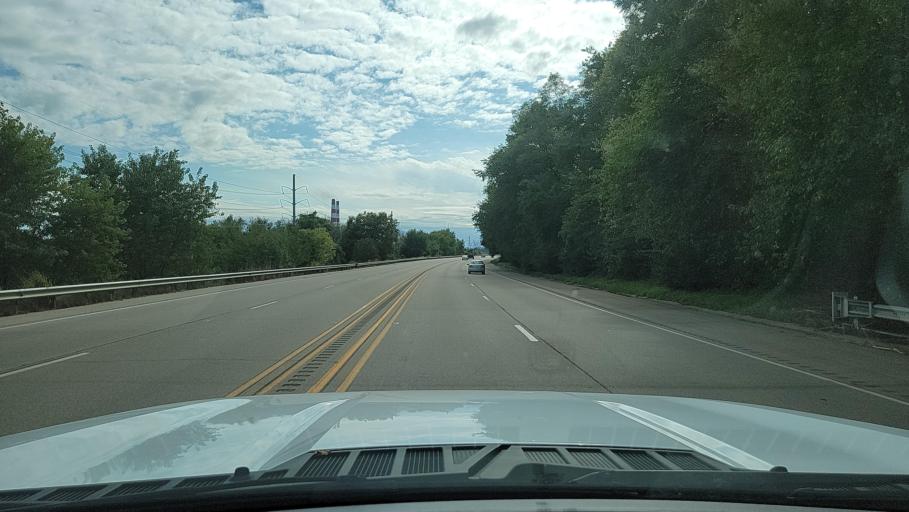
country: US
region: Illinois
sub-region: Tazewell County
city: North Pekin
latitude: 40.6123
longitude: -89.6593
